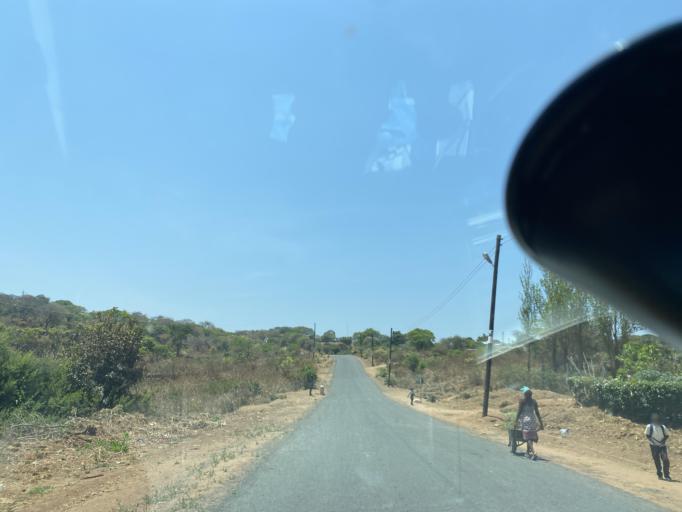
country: ZM
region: Lusaka
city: Kafue
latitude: -15.8676
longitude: 28.4344
